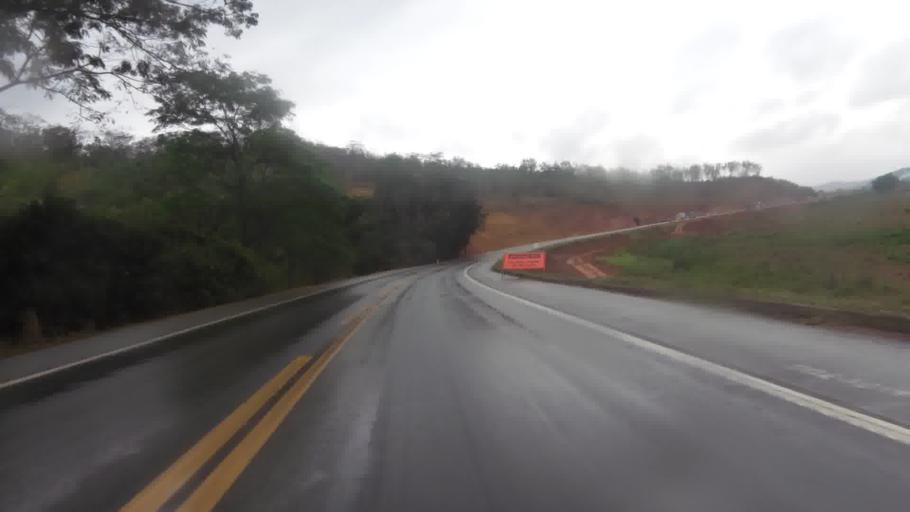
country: BR
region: Espirito Santo
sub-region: Cachoeiro De Itapemirim
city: Cachoeiro de Itapemirim
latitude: -20.8931
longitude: -41.0396
